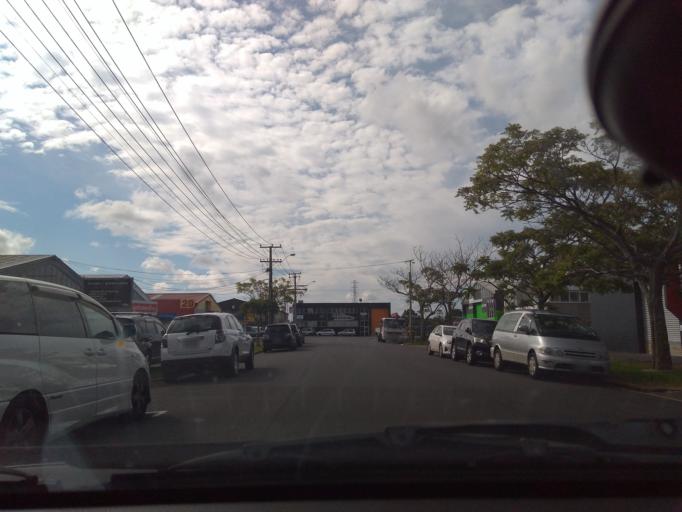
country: NZ
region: Auckland
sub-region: Auckland
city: Rosebank
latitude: -36.9028
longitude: 174.6869
